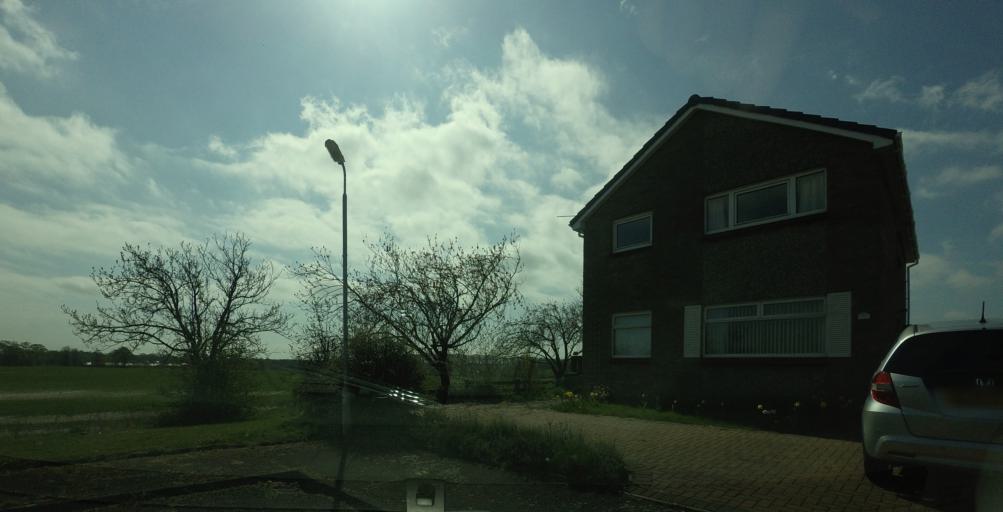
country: GB
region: Scotland
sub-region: Fife
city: Crossford
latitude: 56.0569
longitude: -3.4970
